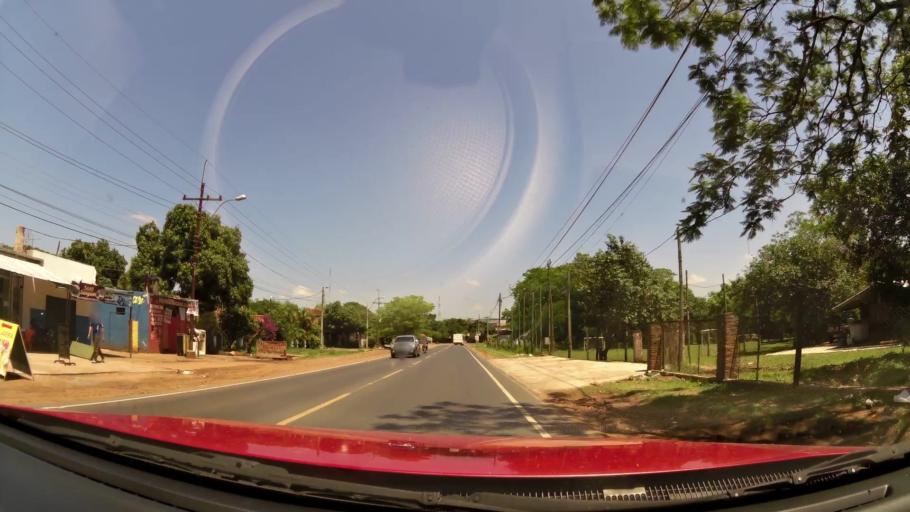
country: PY
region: Central
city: Nemby
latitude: -25.3978
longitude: -57.5334
